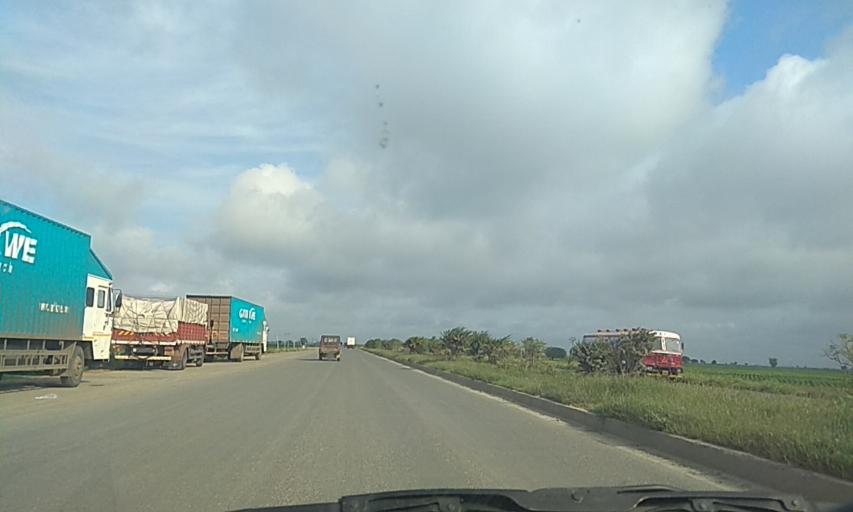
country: IN
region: Karnataka
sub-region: Haveri
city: Savanur
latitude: 14.8881
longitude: 75.3021
